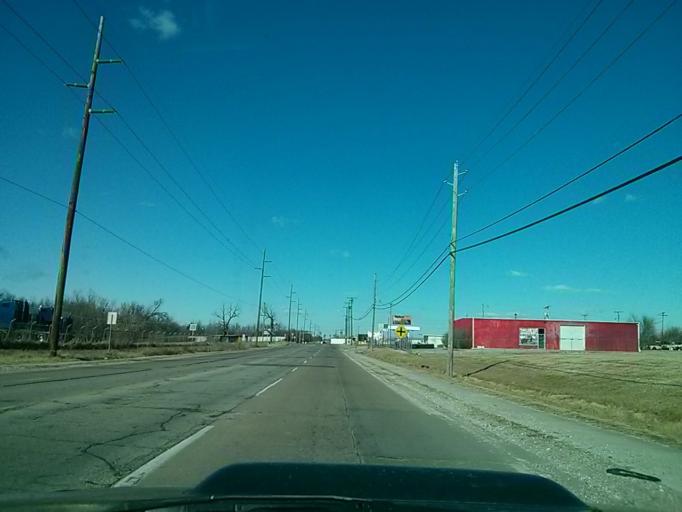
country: US
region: Oklahoma
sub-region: Tulsa County
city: Turley
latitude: 36.2029
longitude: -95.9582
